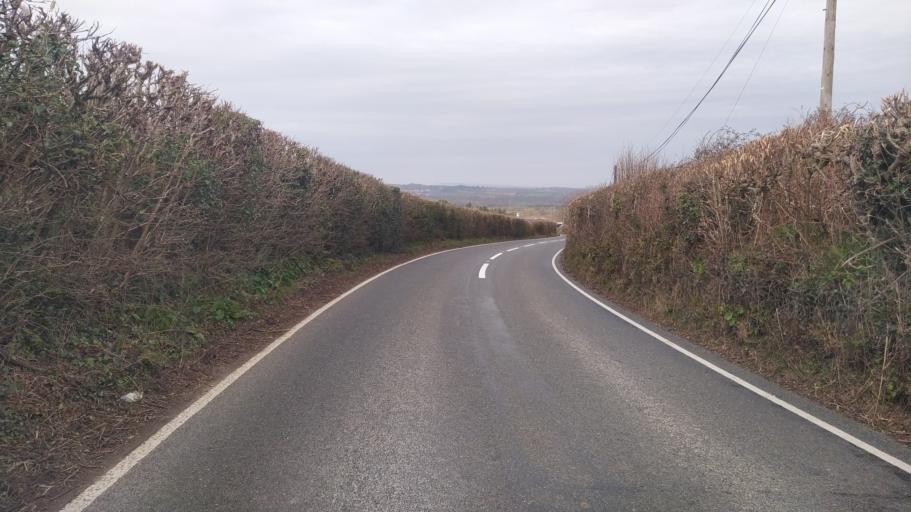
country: GB
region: England
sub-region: Dorset
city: Beaminster
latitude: 50.8563
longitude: -2.7317
